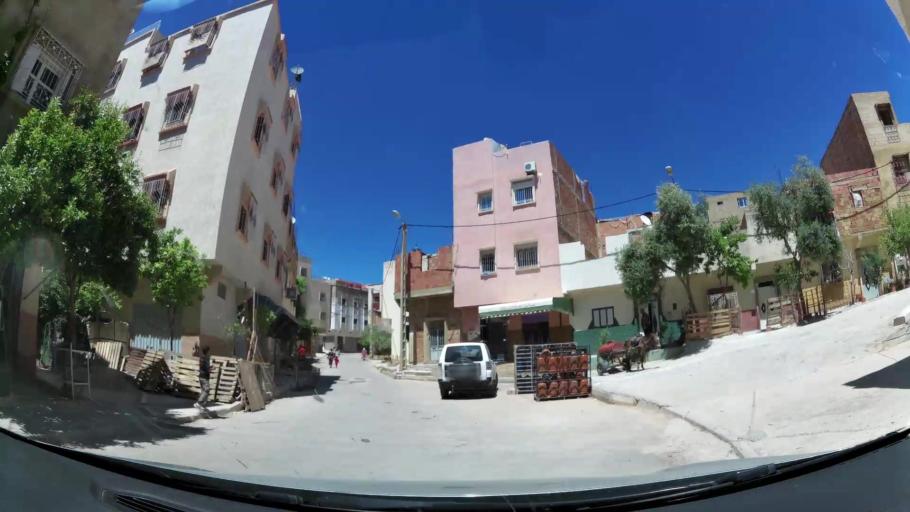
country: MA
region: Meknes-Tafilalet
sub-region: Meknes
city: Meknes
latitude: 33.9071
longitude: -5.5789
